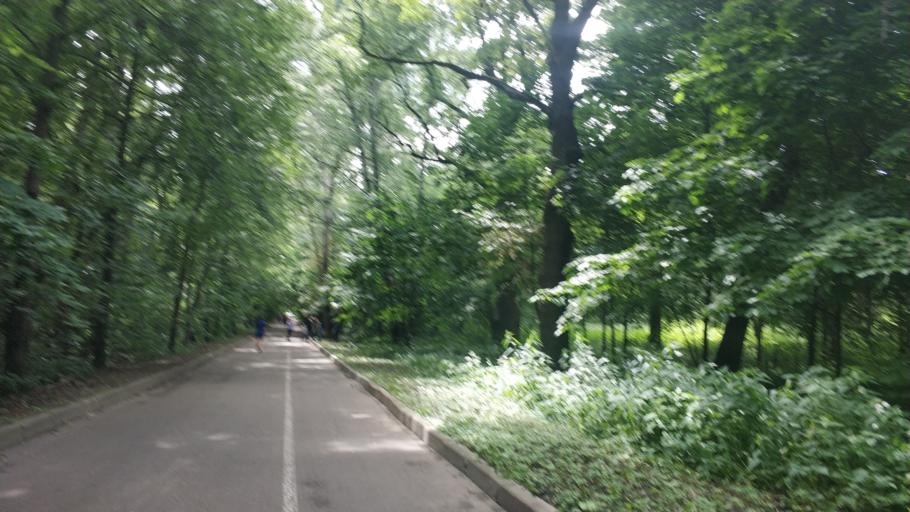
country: RU
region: Moscow
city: Perovo
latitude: 55.7395
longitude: 37.8025
